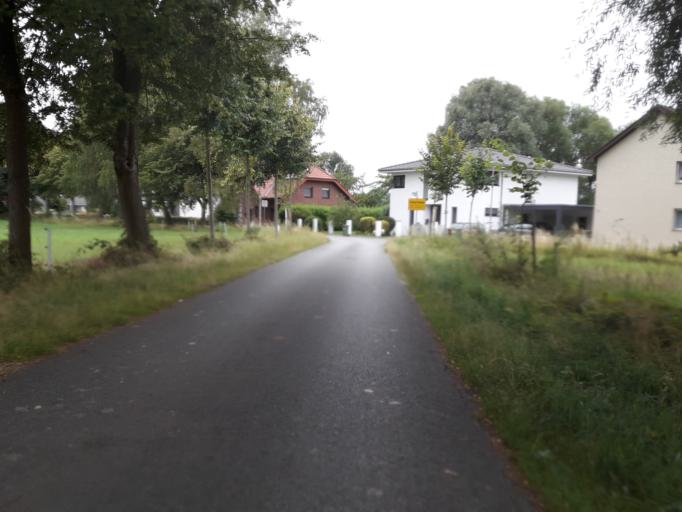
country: DE
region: North Rhine-Westphalia
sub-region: Regierungsbezirk Detmold
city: Salzkotten
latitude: 51.7210
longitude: 8.6336
